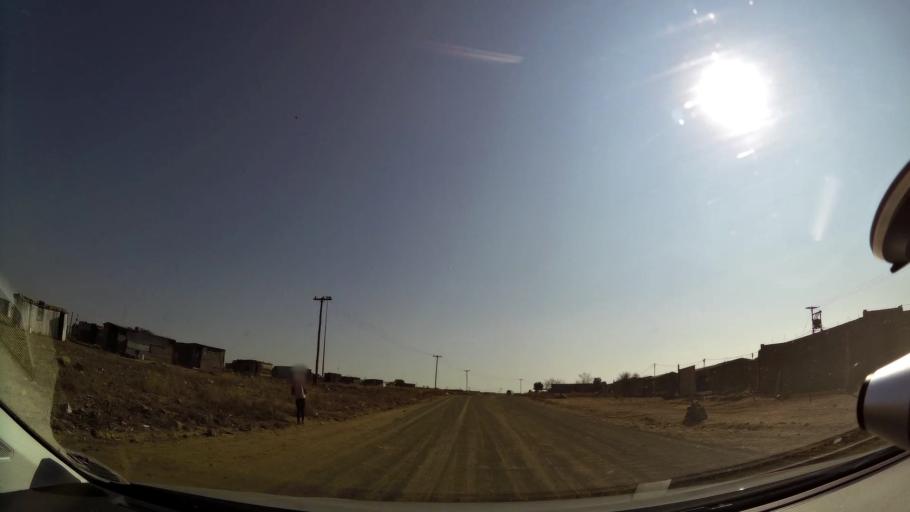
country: ZA
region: Orange Free State
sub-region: Mangaung Metropolitan Municipality
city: Bloemfontein
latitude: -29.1856
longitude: 26.2853
